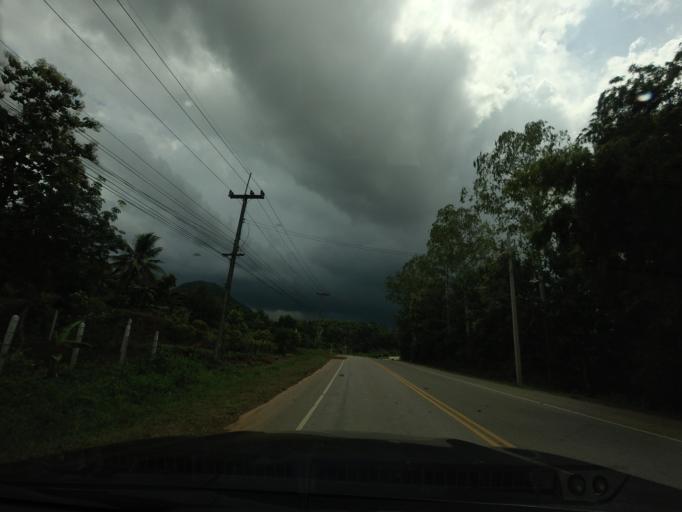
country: LA
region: Vientiane
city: Muang Sanakham
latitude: 17.9794
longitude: 101.7478
